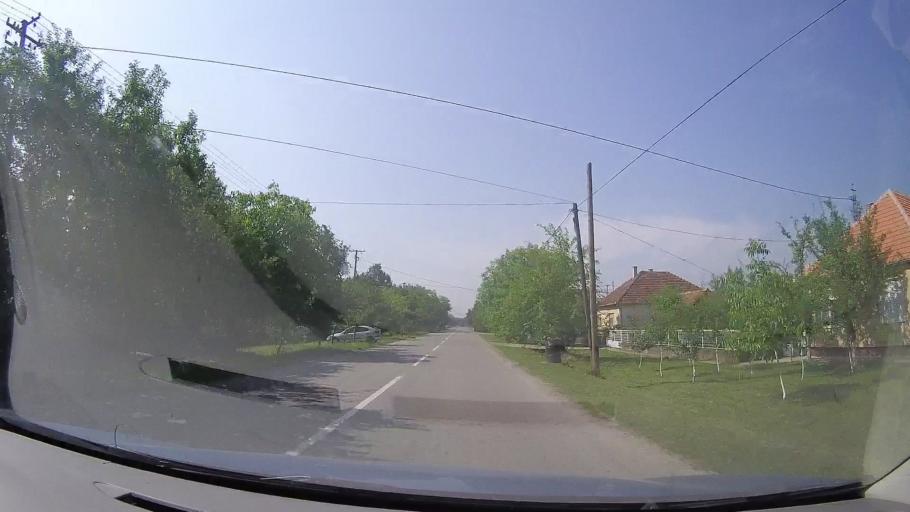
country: RS
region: Autonomna Pokrajina Vojvodina
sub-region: Srednjebanatski Okrug
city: Secanj
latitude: 45.3729
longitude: 20.7778
